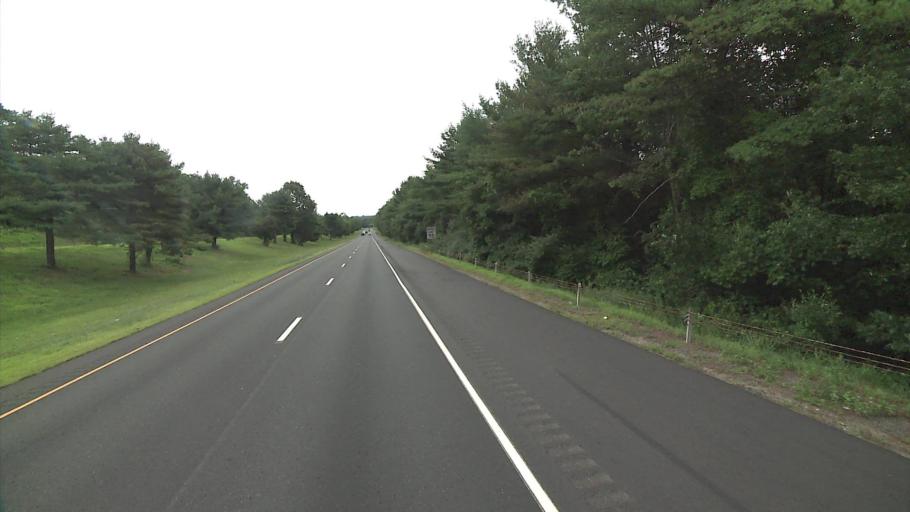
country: US
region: Connecticut
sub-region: Fairfield County
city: Trumbull
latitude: 41.2586
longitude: -73.1407
